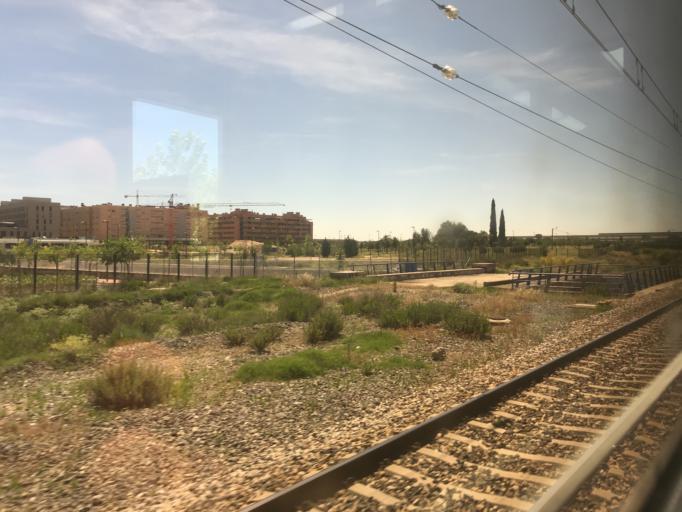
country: ES
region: Madrid
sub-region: Provincia de Madrid
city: Getafe
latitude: 40.3174
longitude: -3.7096
